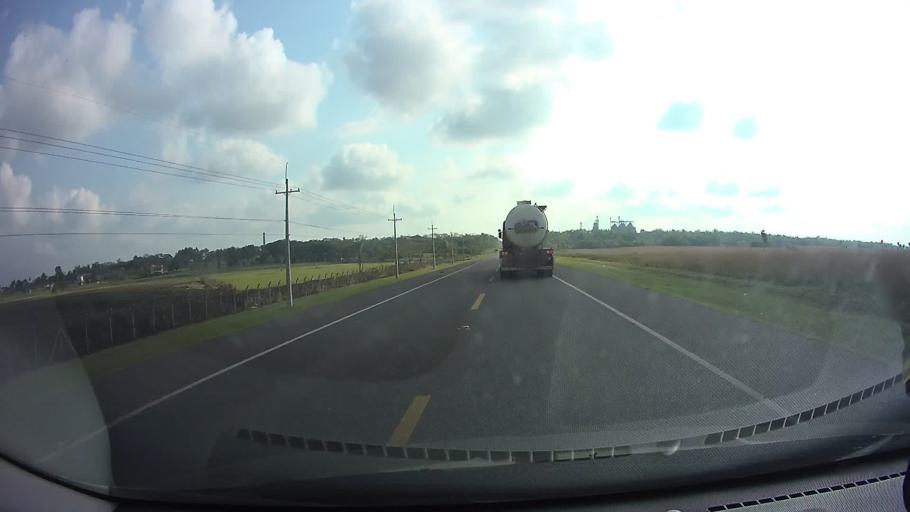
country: PY
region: Cordillera
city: Arroyos y Esteros
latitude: -25.0642
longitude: -57.1985
